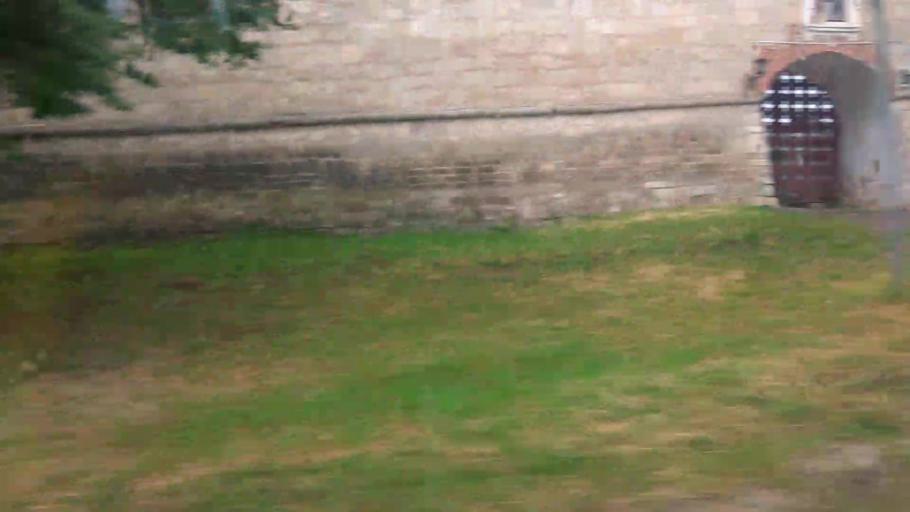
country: RU
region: Moskovskaya
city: Zaraysk
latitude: 54.7572
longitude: 38.8734
